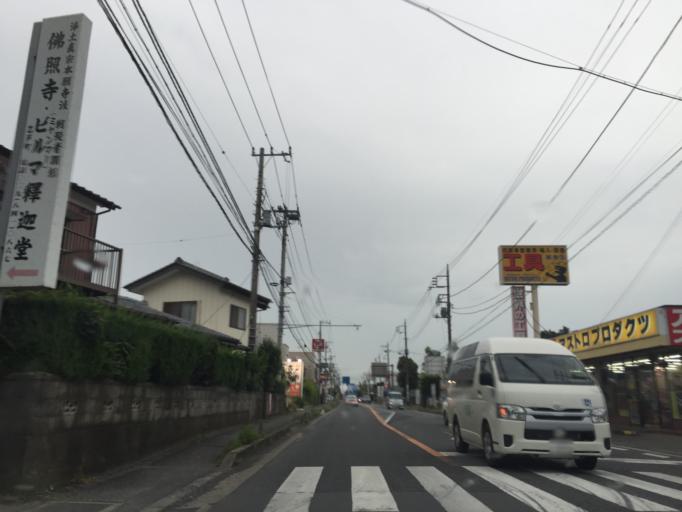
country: JP
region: Ibaraki
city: Naka
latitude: 36.0306
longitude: 140.1613
